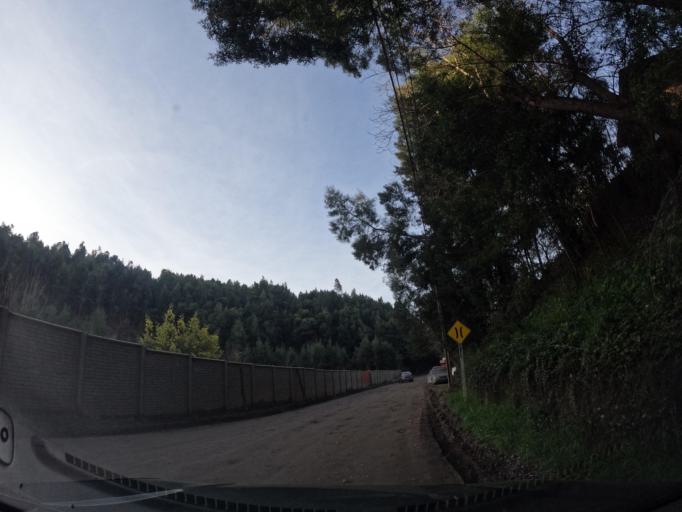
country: CL
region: Biobio
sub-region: Provincia de Concepcion
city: Concepcion
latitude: -36.8480
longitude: -73.0087
